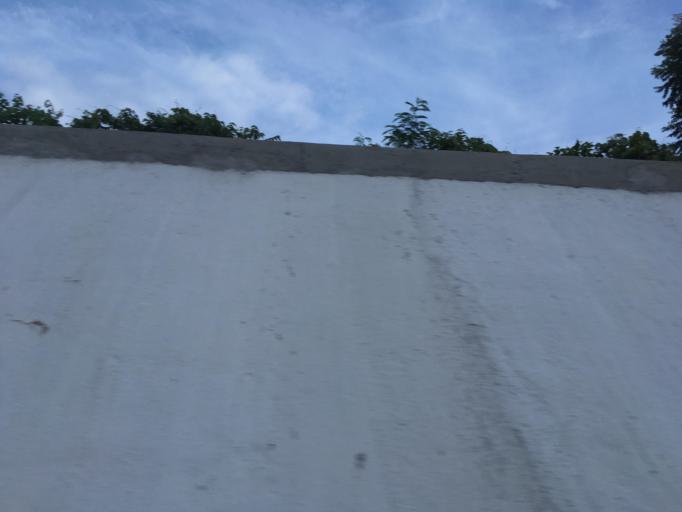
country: TW
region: Taiwan
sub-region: Yilan
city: Yilan
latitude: 24.4449
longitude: 121.7793
